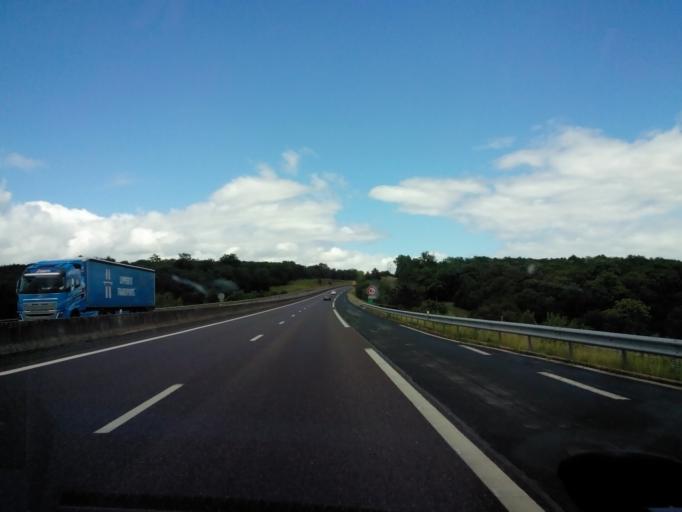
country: FR
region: Lorraine
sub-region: Departement de Meurthe-et-Moselle
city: Colombey-les-Belles
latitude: 48.4610
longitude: 5.8706
